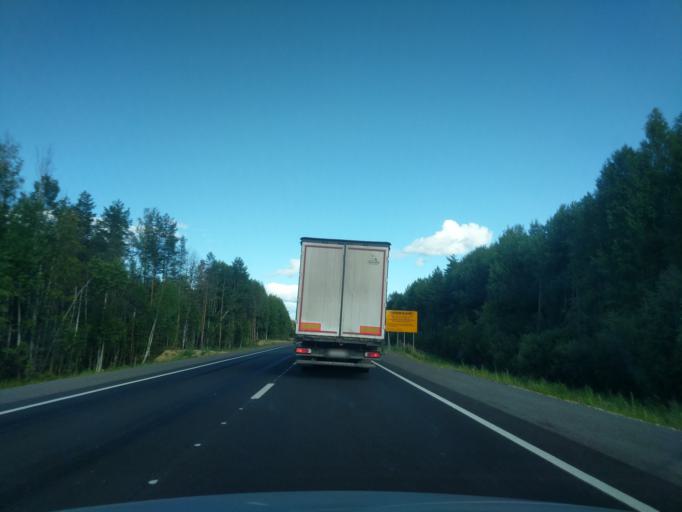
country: RU
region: Kostroma
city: Makar'yev
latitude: 57.8482
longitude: 43.6721
